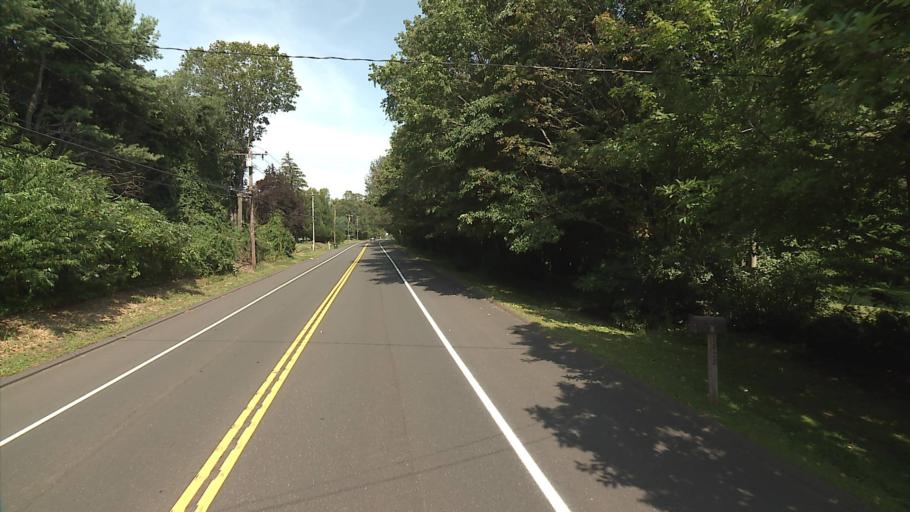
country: US
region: Connecticut
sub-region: New Haven County
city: Guilford
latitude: 41.3691
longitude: -72.6384
